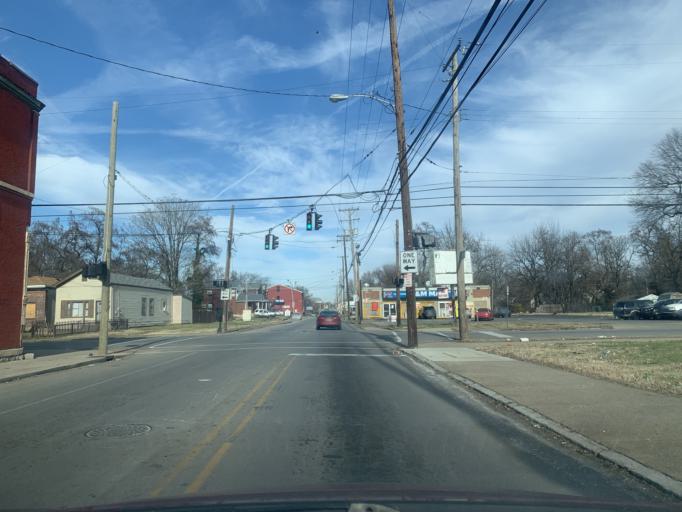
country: US
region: Kentucky
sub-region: Jefferson County
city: Louisville
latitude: 38.2550
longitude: -85.7943
